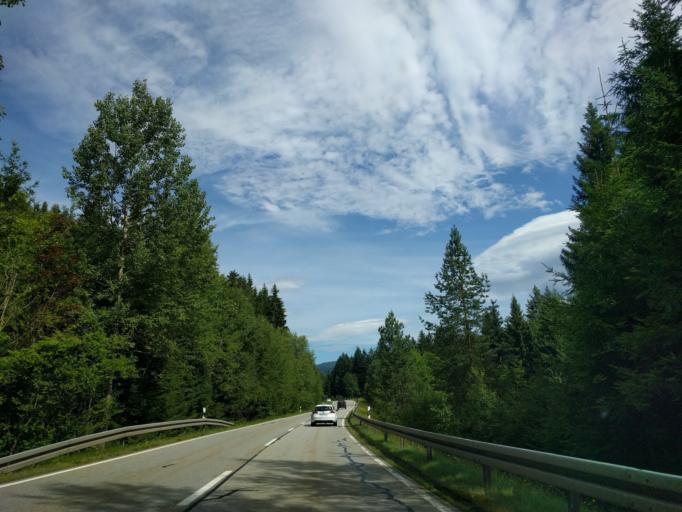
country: DE
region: Bavaria
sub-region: Lower Bavaria
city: Bodenmais
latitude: 49.0417
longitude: 13.1157
